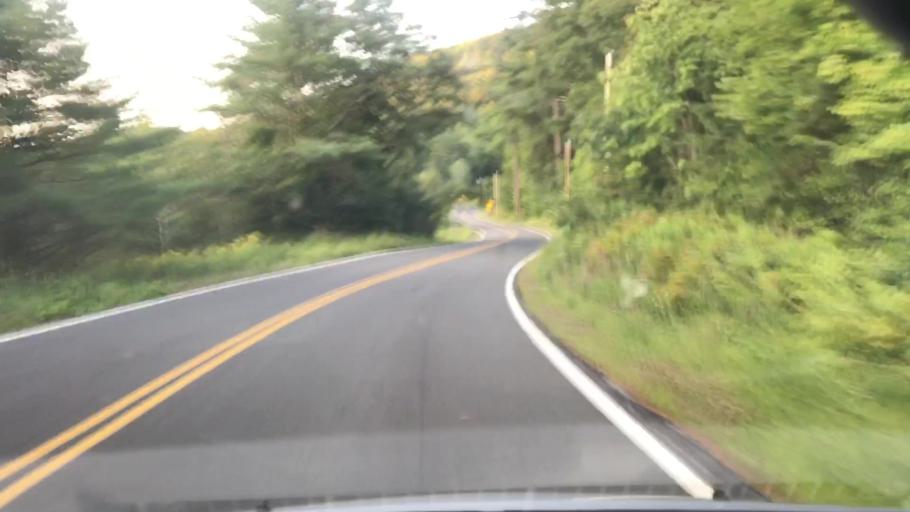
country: US
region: New Hampshire
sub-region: Grafton County
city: Woodsville
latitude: 44.1662
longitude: -72.0461
